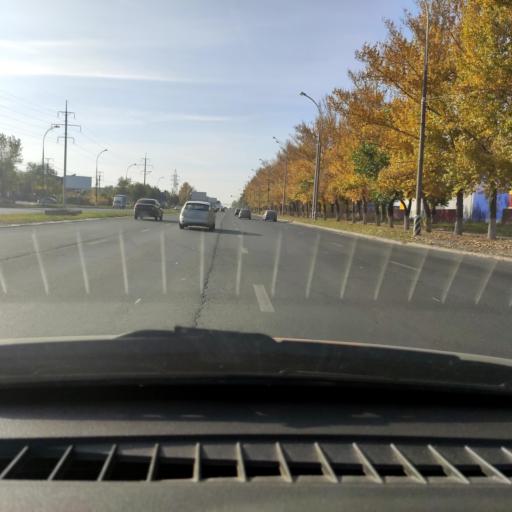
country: RU
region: Samara
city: Tol'yatti
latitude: 53.5492
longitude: 49.2864
